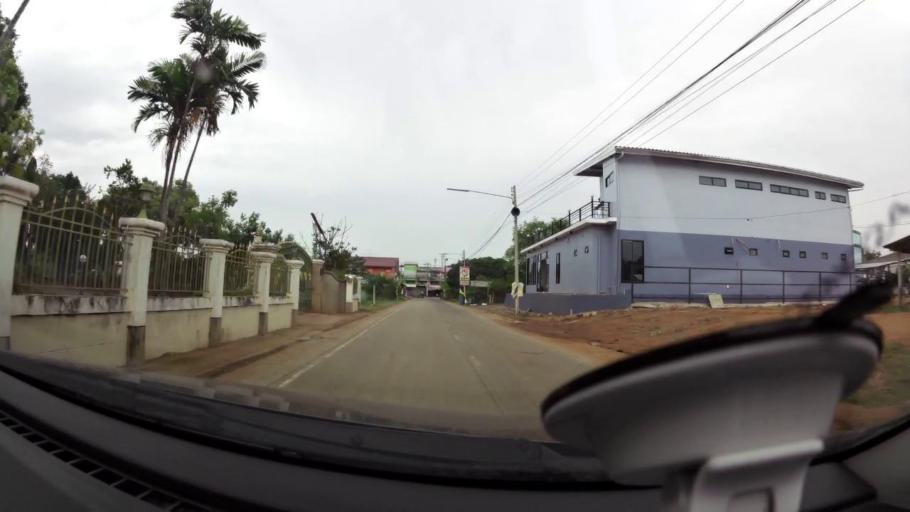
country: TH
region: Prachuap Khiri Khan
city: Pran Buri
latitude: 12.3906
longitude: 99.9850
